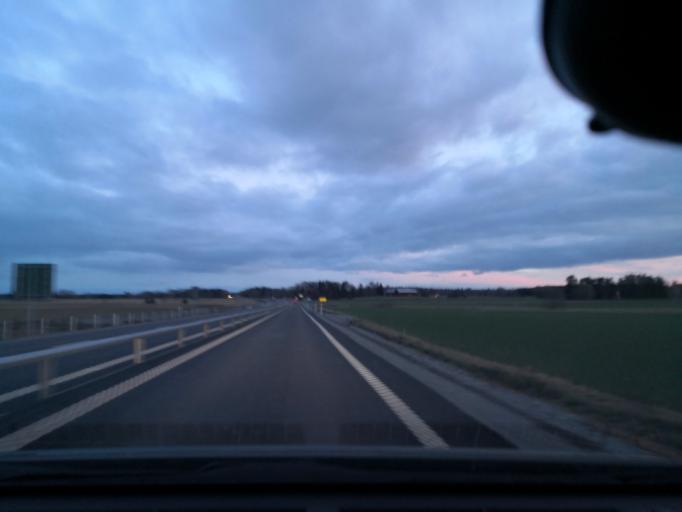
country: SE
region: Uppsala
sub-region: Enkopings Kommun
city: Enkoping
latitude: 59.6845
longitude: 17.0387
